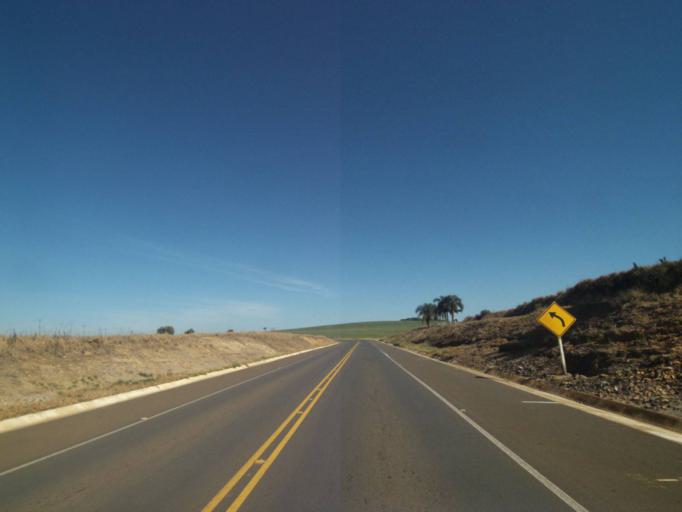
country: BR
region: Parana
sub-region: Tibagi
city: Tibagi
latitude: -24.6320
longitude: -50.4579
